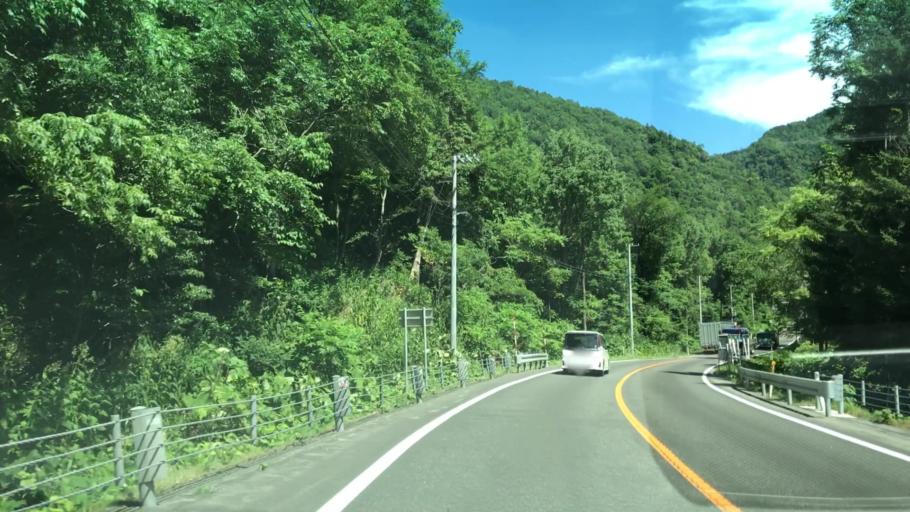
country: JP
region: Hokkaido
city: Shimo-furano
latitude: 42.9306
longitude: 142.5934
